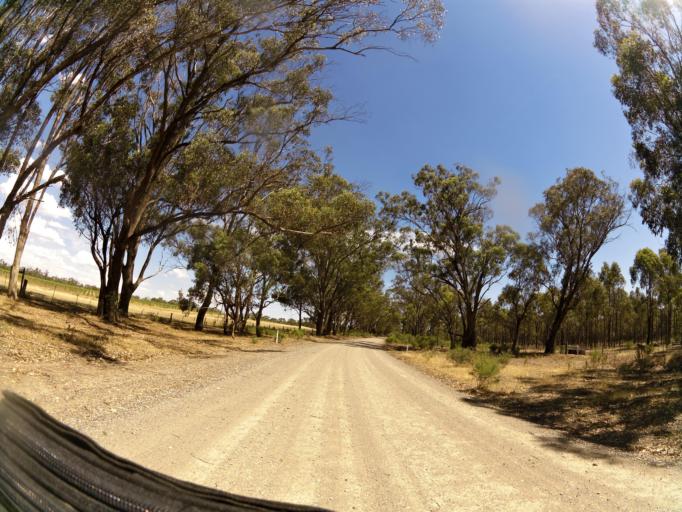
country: AU
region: Victoria
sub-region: Campaspe
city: Kyabram
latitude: -36.8176
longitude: 145.0805
